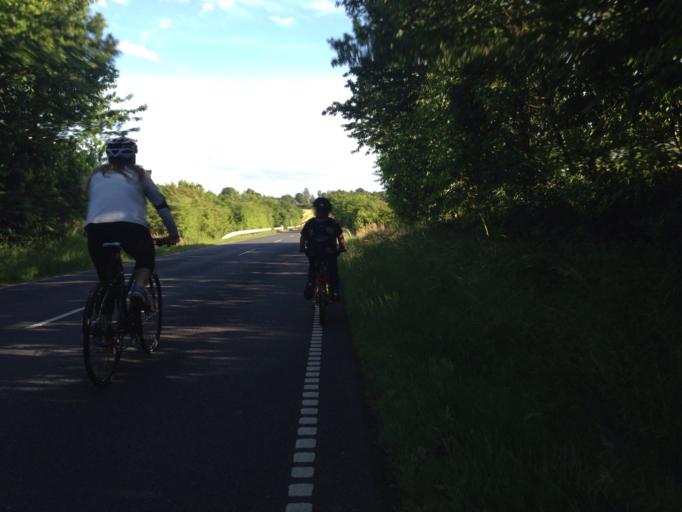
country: DK
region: South Denmark
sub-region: Middelfart Kommune
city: Norre Aby
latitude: 55.4868
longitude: 9.9023
